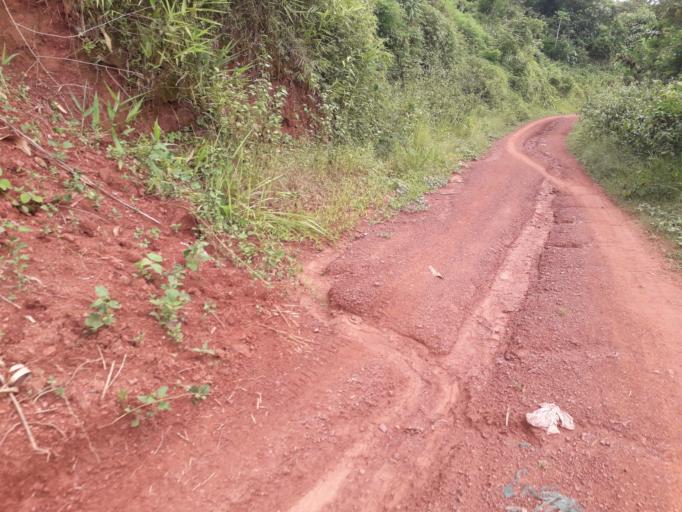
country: CN
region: Yunnan
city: Menglie
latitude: 22.2031
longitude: 101.6716
